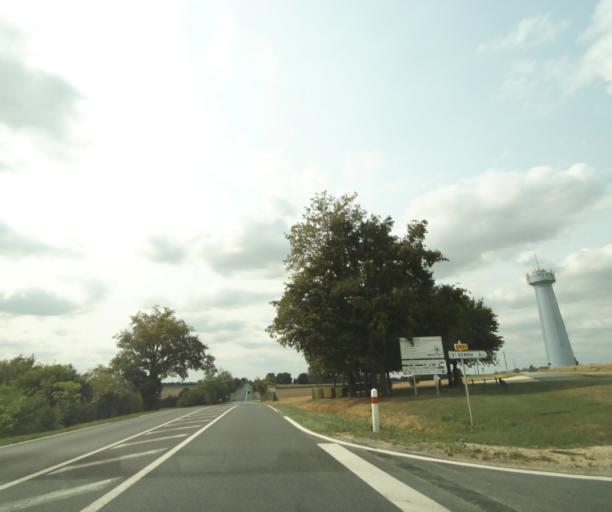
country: FR
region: Centre
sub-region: Departement de l'Indre
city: Buzancais
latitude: 46.9077
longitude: 1.3456
